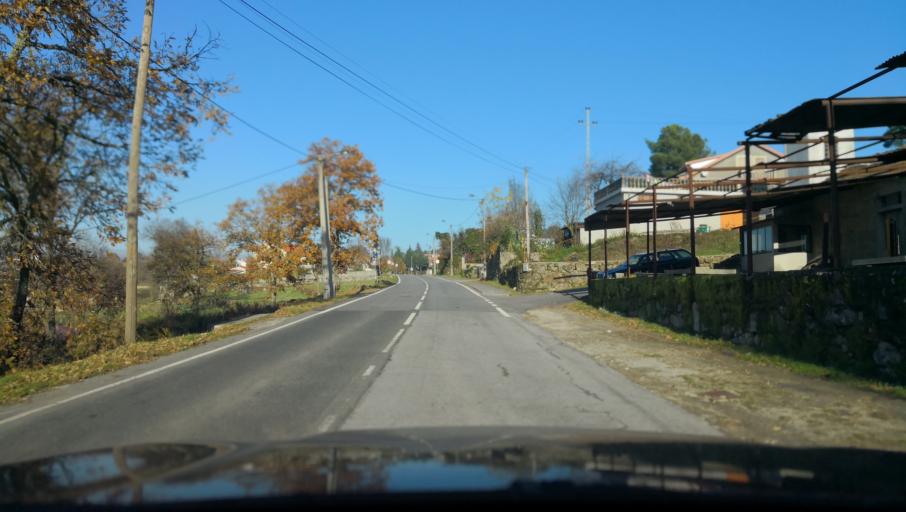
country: PT
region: Vila Real
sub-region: Vila Real
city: Vila Real
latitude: 41.3301
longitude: -7.6676
